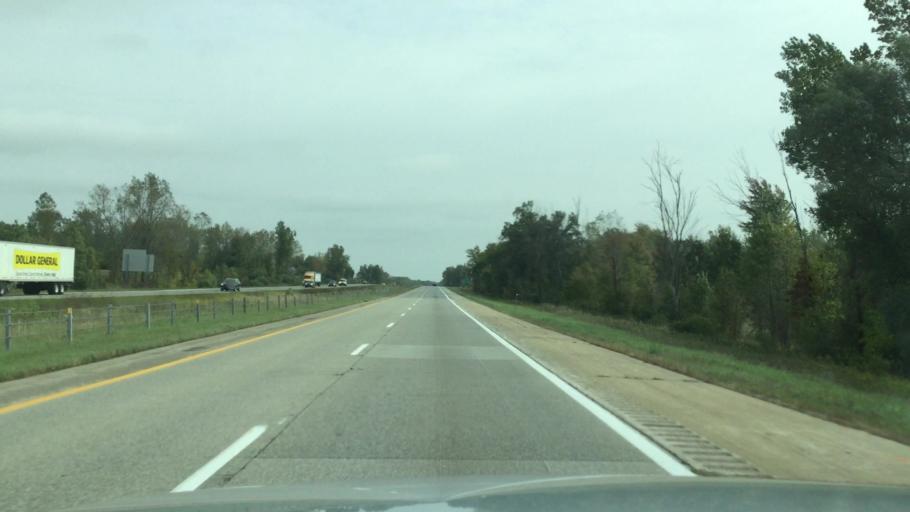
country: US
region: Michigan
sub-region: Shiawassee County
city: Perry
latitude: 42.8442
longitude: -84.1944
